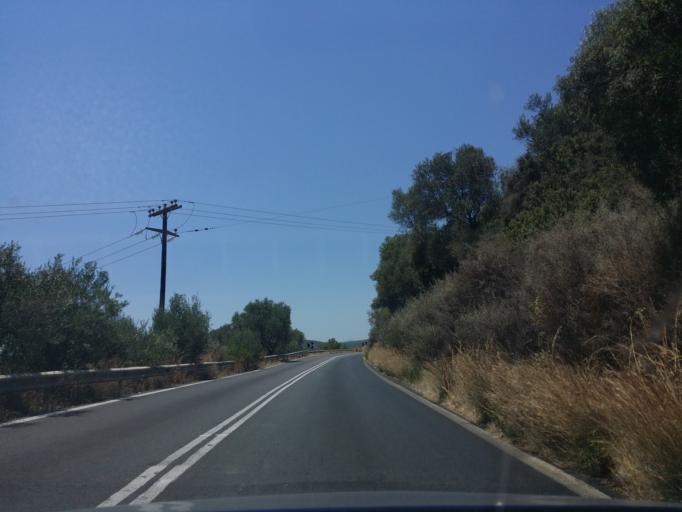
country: GR
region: Peloponnese
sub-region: Nomos Lakonias
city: Skala
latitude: 36.8492
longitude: 22.6216
